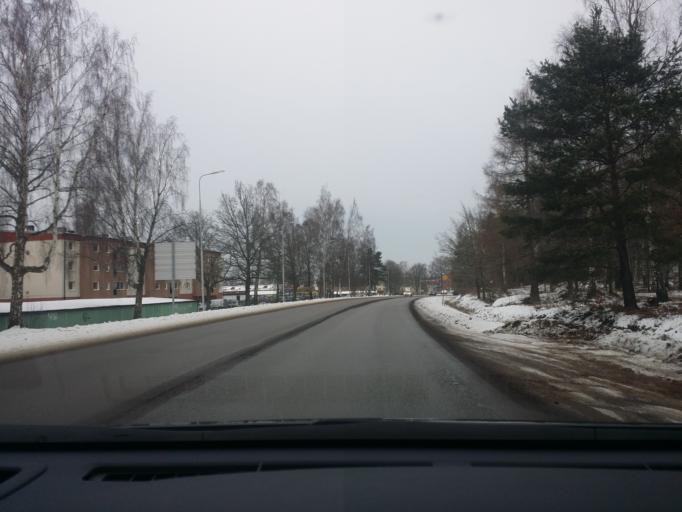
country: SE
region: Vaestra Goetaland
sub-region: Mariestads Kommun
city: Mariestad
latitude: 58.6943
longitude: 13.8157
